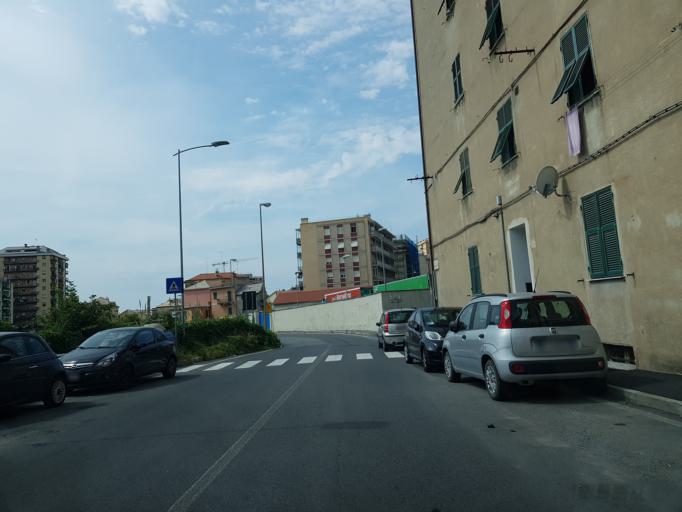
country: IT
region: Liguria
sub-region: Provincia di Genova
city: San Teodoro
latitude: 44.4348
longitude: 8.8545
